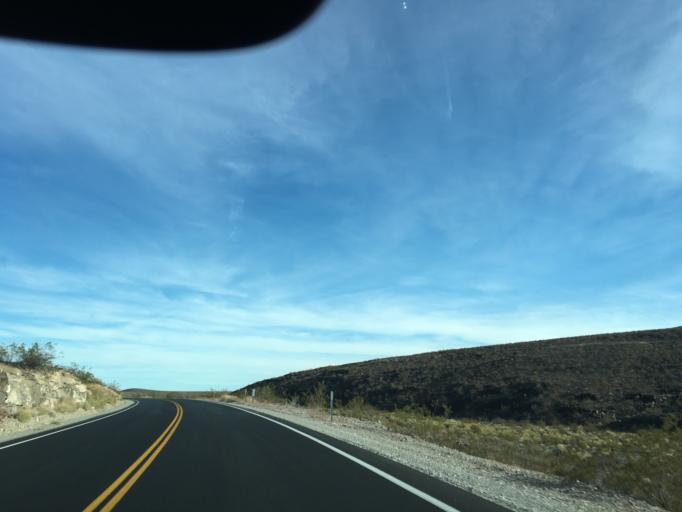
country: US
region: Nevada
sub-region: Nye County
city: Beatty
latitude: 36.3532
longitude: -116.6430
